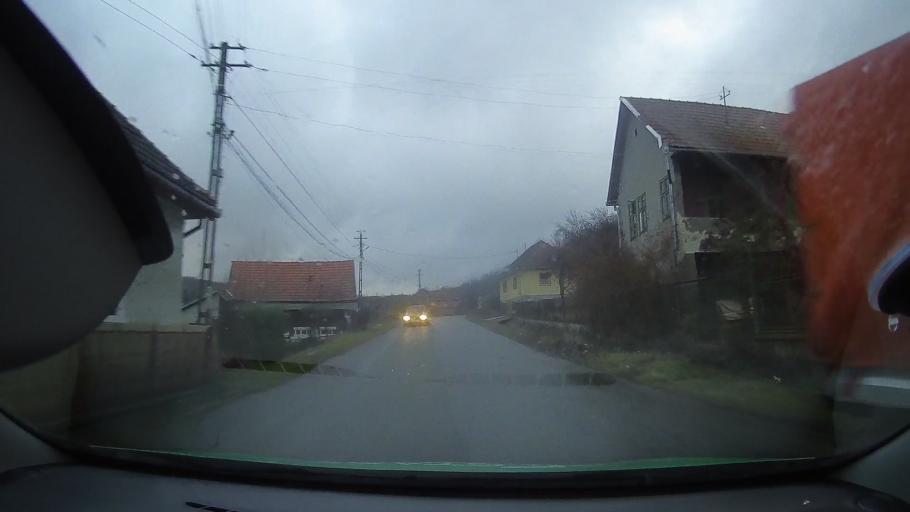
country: RO
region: Hunedoara
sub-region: Comuna Baia de Cris
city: Baia de Cris
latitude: 46.2123
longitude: 22.7144
